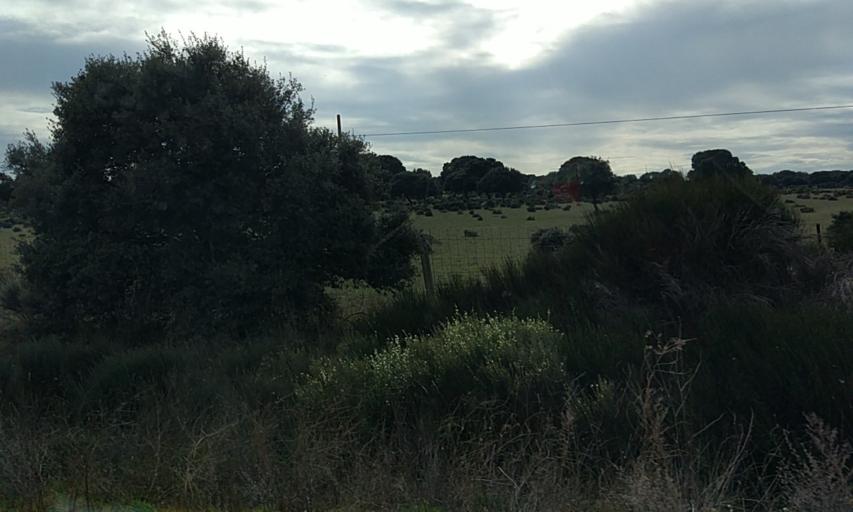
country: ES
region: Castille and Leon
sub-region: Provincia de Salamanca
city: Herguijuela de Ciudad Rodrigo
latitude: 40.4561
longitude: -6.5902
